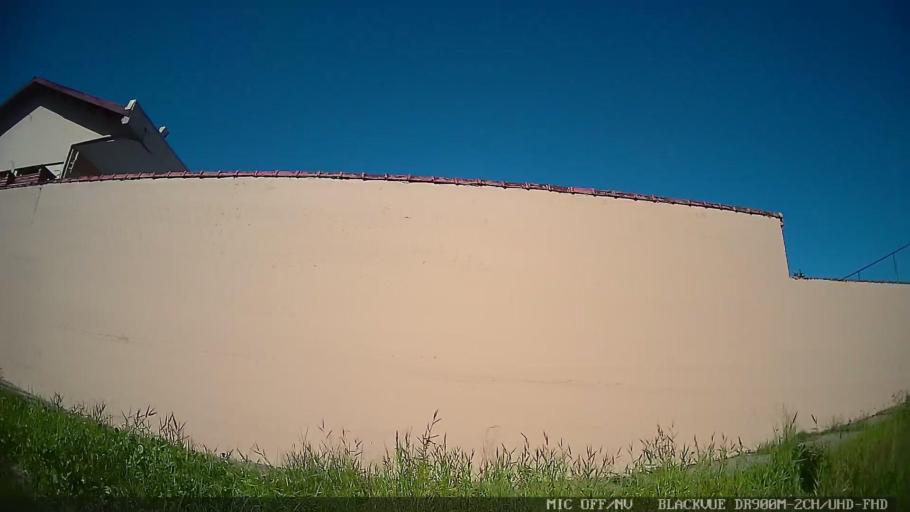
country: BR
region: Sao Paulo
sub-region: Peruibe
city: Peruibe
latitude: -24.2758
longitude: -46.9491
